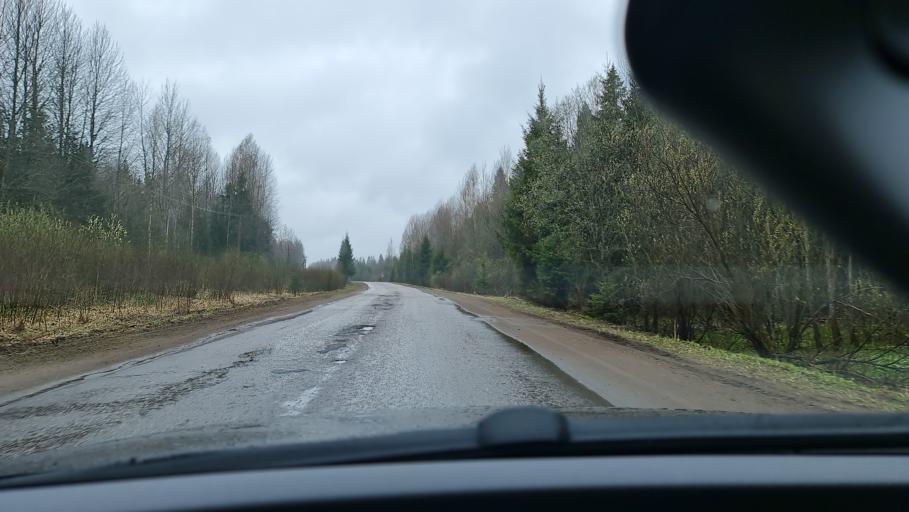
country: RU
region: Novgorod
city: Kresttsy
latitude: 58.0319
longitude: 32.8190
